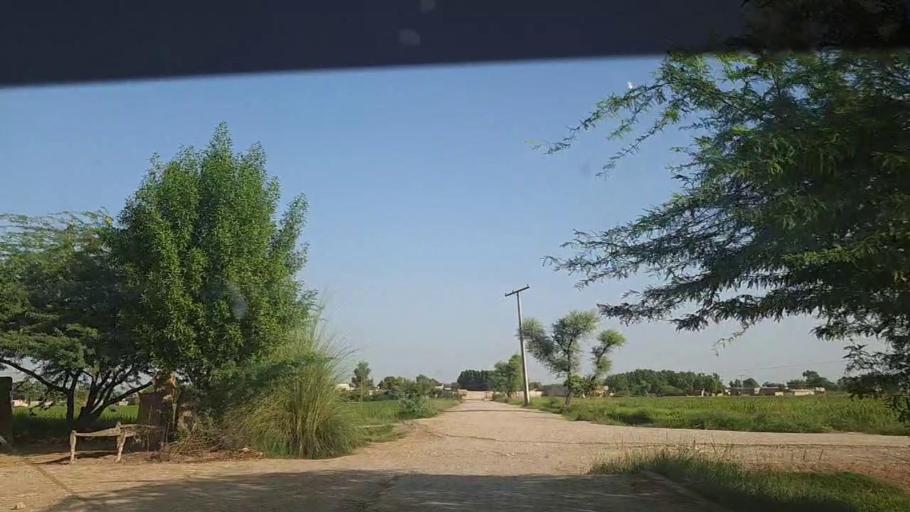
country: PK
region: Sindh
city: Tangwani
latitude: 28.2663
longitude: 69.0128
